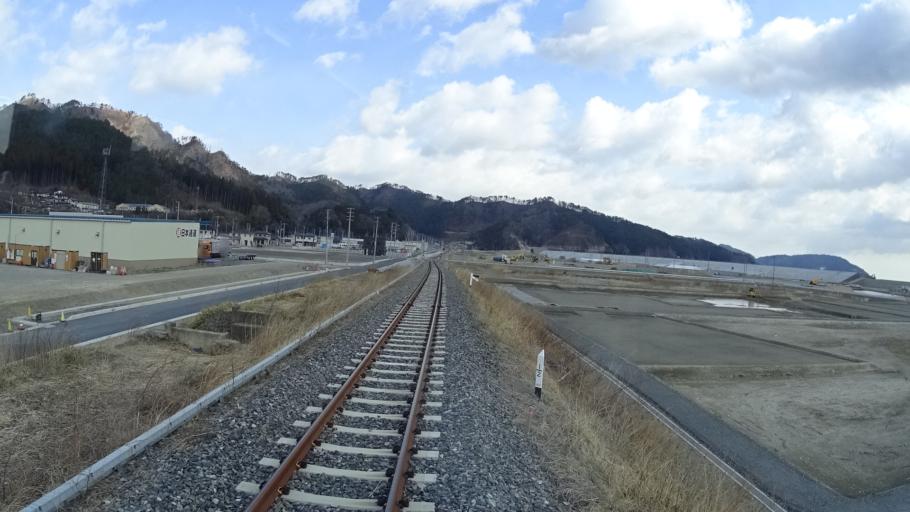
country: JP
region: Iwate
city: Otsuchi
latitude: 39.3308
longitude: 141.8900
